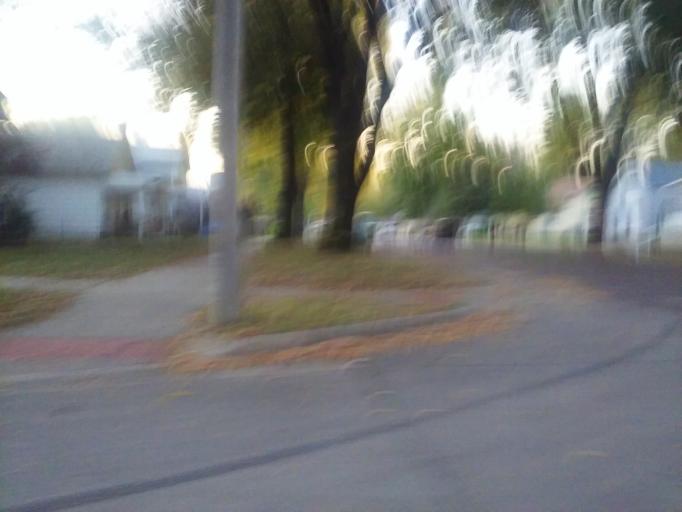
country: US
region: Iowa
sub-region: Linn County
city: Cedar Rapids
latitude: 41.9747
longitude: -91.6525
